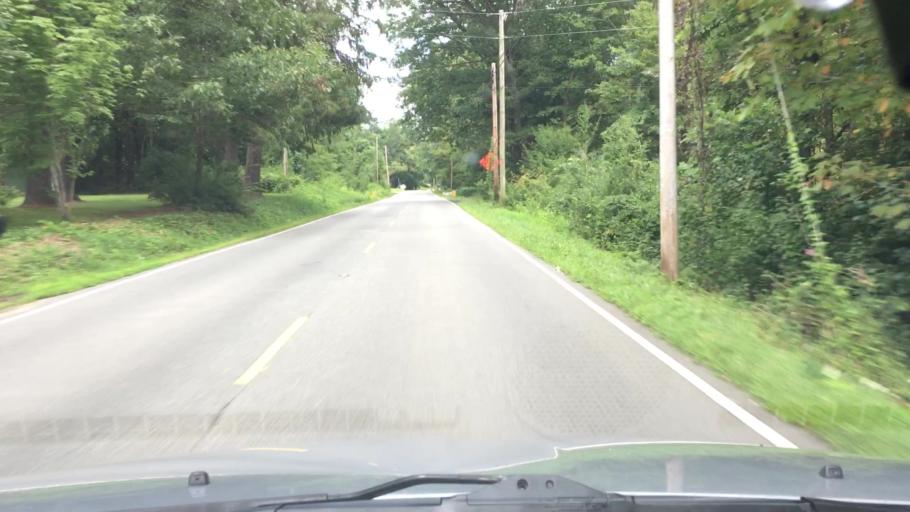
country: US
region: North Carolina
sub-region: Yancey County
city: Burnsville
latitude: 35.8216
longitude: -82.1906
